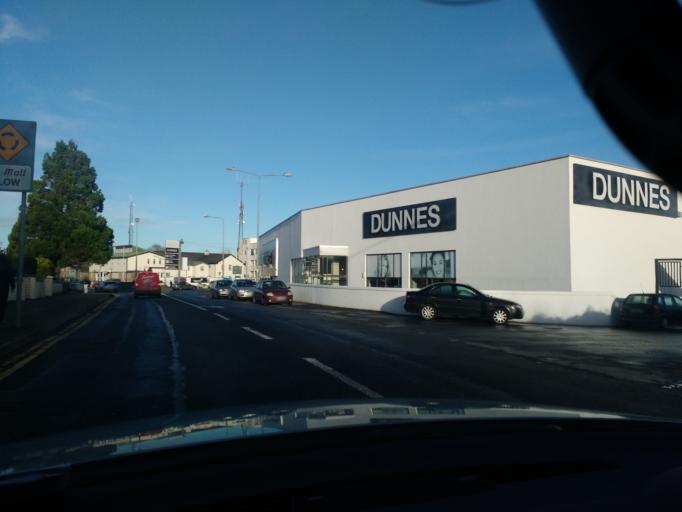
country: IE
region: Munster
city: Thurles
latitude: 52.6744
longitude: -7.8122
